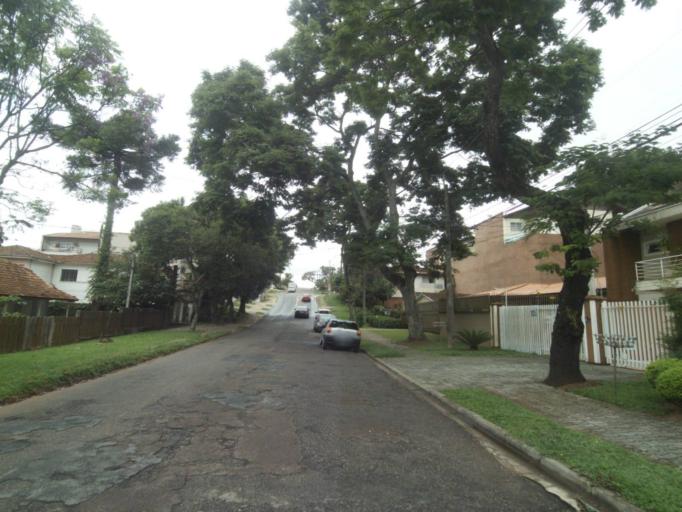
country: BR
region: Parana
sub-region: Curitiba
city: Curitiba
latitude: -25.4127
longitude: -49.2840
